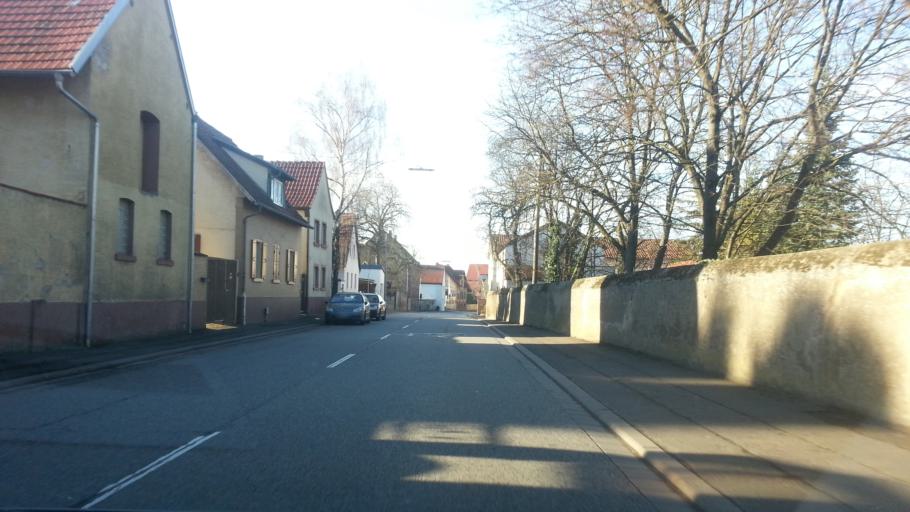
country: DE
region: Rheinland-Pfalz
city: Molsheim
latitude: 49.6363
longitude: 8.1676
